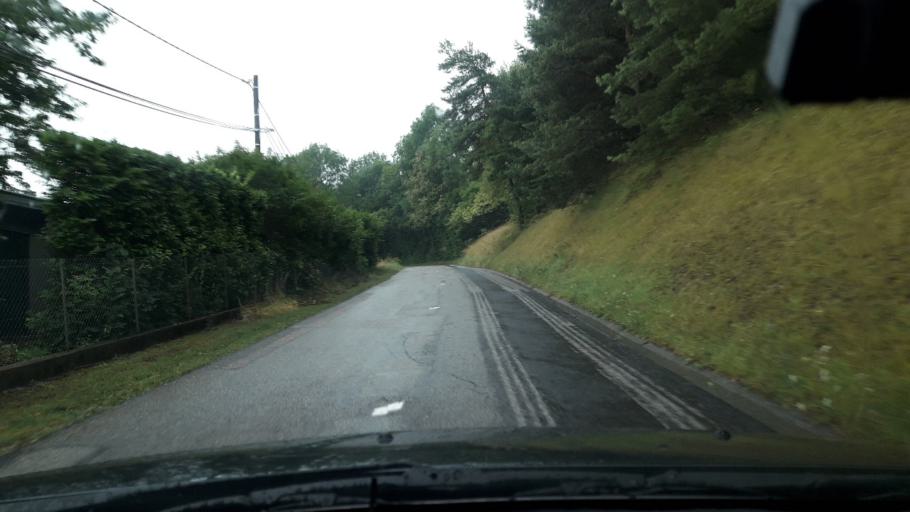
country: FR
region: Rhone-Alpes
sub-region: Departement de la Savoie
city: Saint-Baldoph
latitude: 45.5303
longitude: 5.9394
